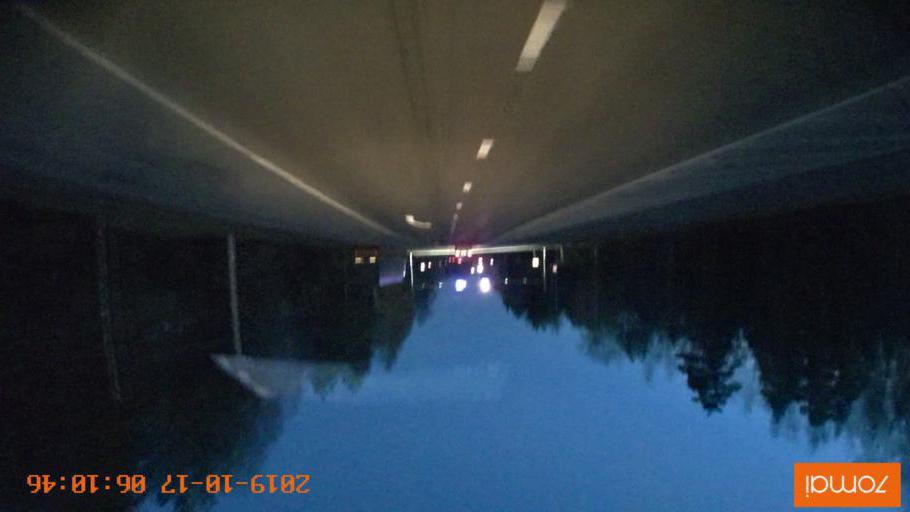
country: RU
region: Ivanovo
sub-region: Gorod Ivanovo
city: Ivanovo
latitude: 56.9286
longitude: 40.9621
